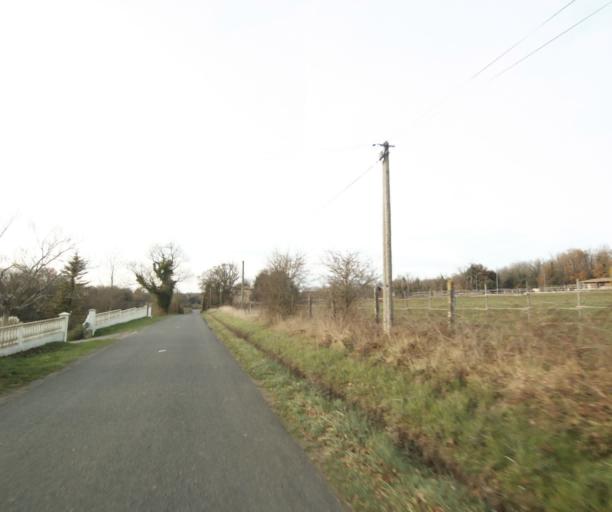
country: FR
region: Poitou-Charentes
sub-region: Departement de la Charente-Maritime
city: Saint-Hilaire-de-Villefranche
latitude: 45.8183
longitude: -0.5564
